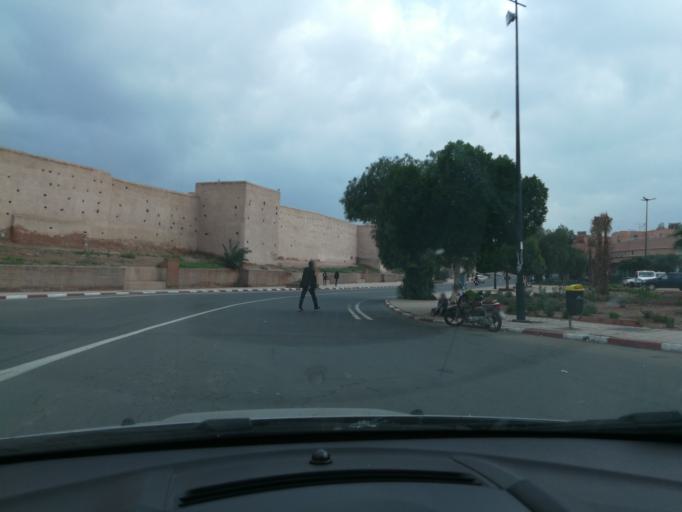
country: MA
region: Marrakech-Tensift-Al Haouz
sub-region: Marrakech
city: Marrakesh
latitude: 31.6330
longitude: -8.0000
